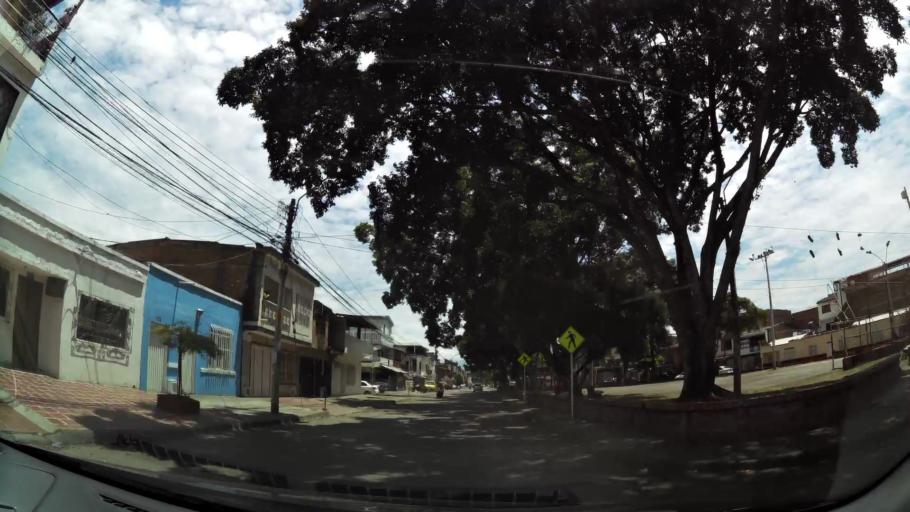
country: CO
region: Valle del Cauca
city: Cali
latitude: 3.4435
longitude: -76.5041
